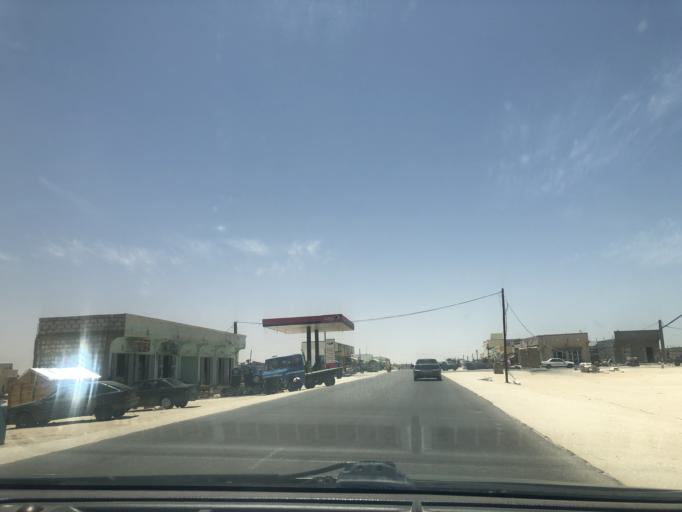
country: MR
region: Nouakchott
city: Nouakchott
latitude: 18.0152
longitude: -15.9590
